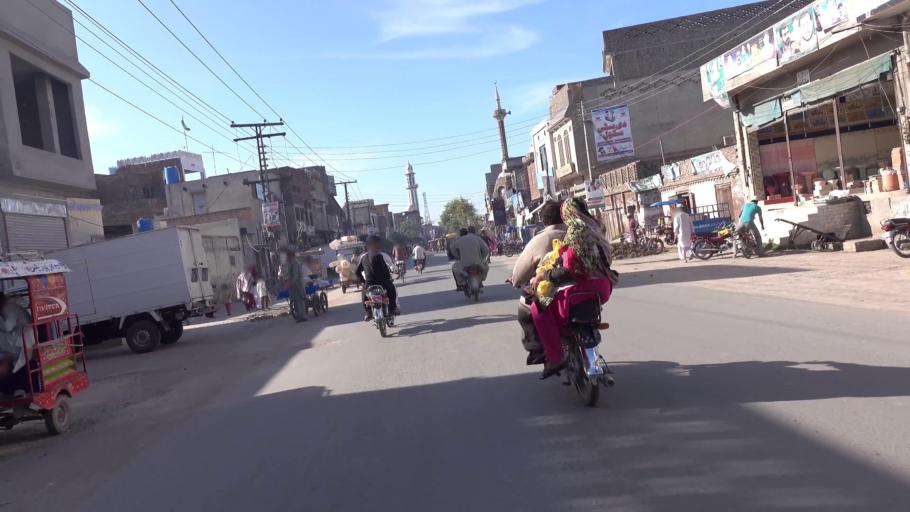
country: PK
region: Punjab
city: Hafizabad
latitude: 32.0741
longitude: 73.6858
